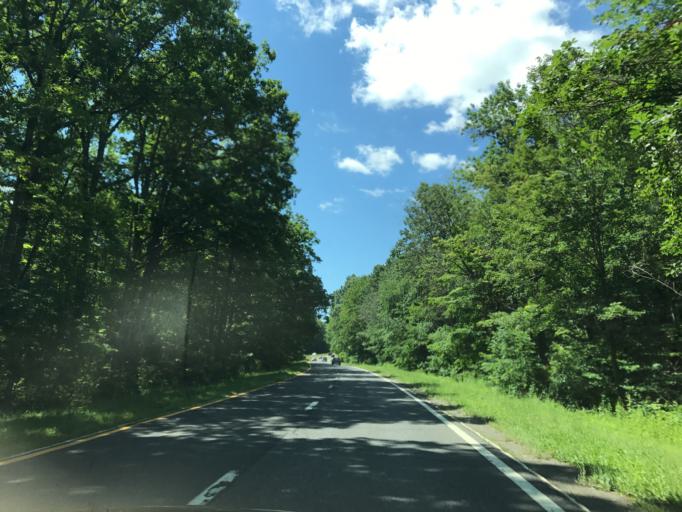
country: US
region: New York
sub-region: Dutchess County
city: Millbrook
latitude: 41.8081
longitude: -73.7655
